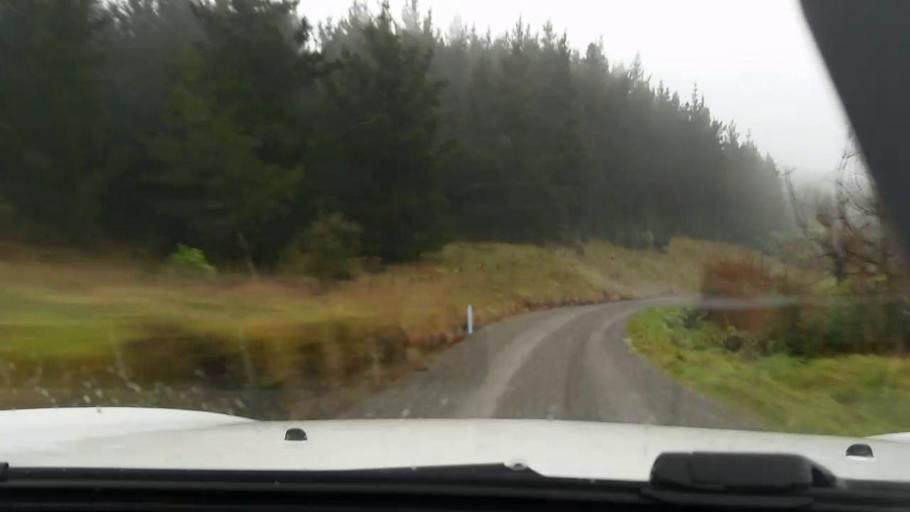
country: NZ
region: Wellington
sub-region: Masterton District
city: Masterton
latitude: -41.1892
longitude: 175.8175
